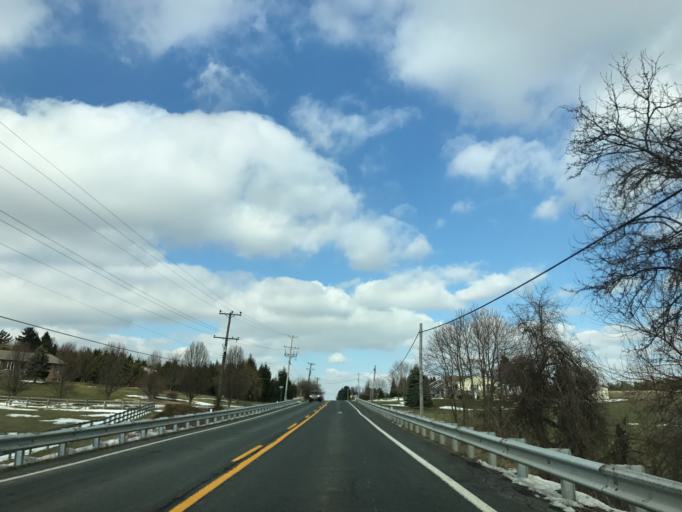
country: US
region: Maryland
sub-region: Carroll County
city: Manchester
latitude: 39.6958
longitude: -76.9080
